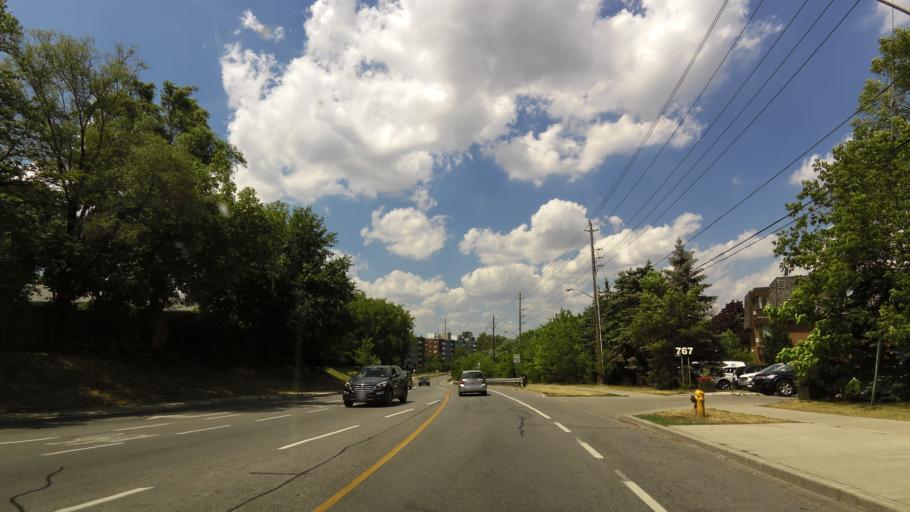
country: CA
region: Ontario
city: Etobicoke
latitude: 43.6372
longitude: -79.5071
